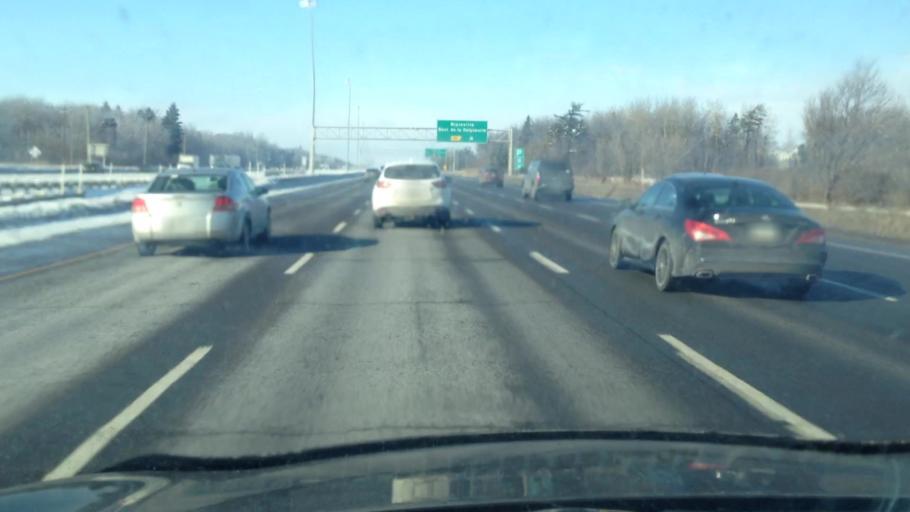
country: CA
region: Quebec
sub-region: Laurentides
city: Blainville
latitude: 45.6534
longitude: -73.8780
